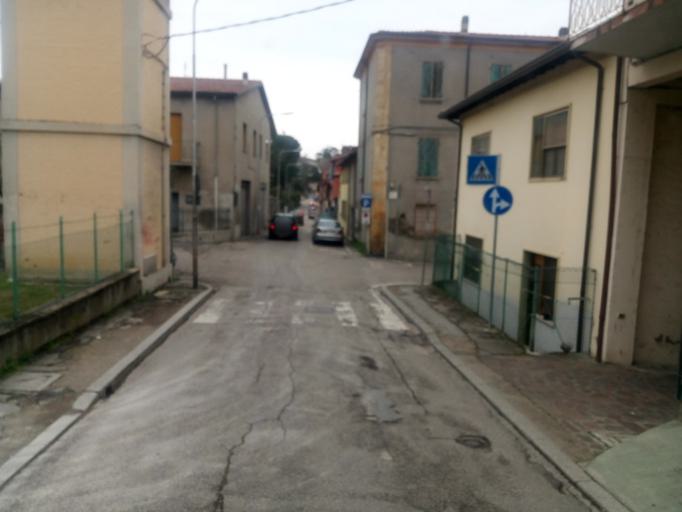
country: IT
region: Emilia-Romagna
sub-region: Forli-Cesena
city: Meldola
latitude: 44.1237
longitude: 12.0594
